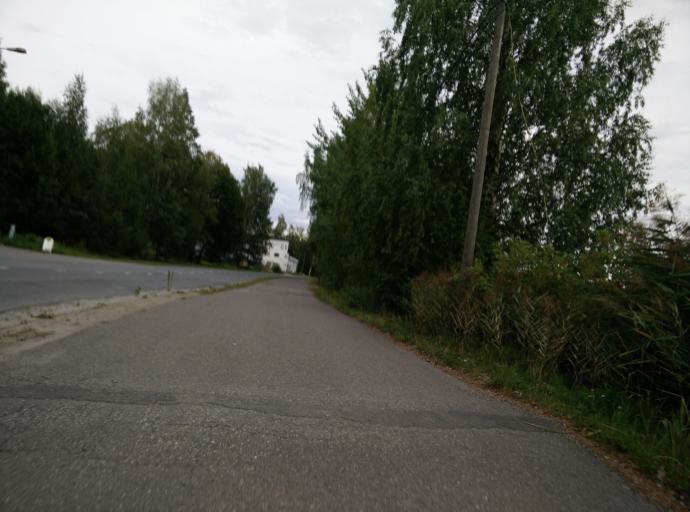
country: FI
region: Haeme
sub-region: Haemeenlinna
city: Haemeenlinna
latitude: 60.9936
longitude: 24.4887
